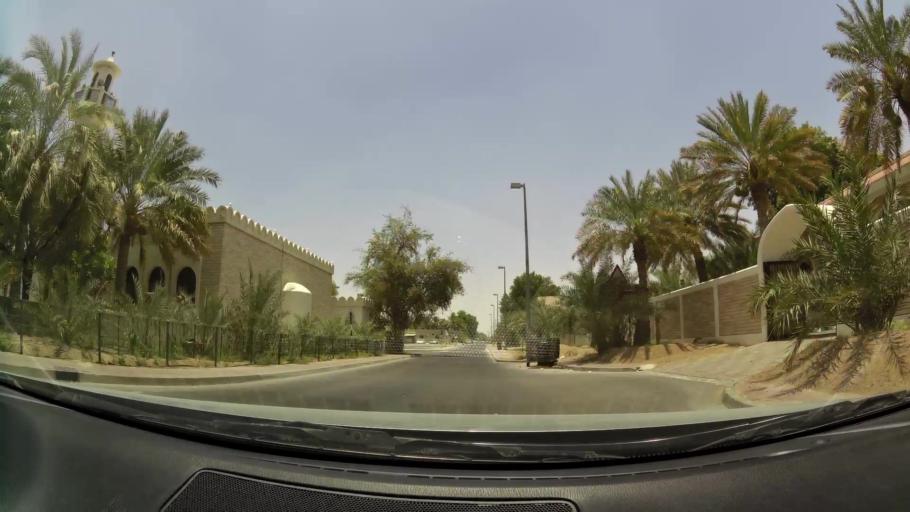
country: OM
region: Al Buraimi
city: Al Buraymi
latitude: 24.2671
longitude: 55.7366
